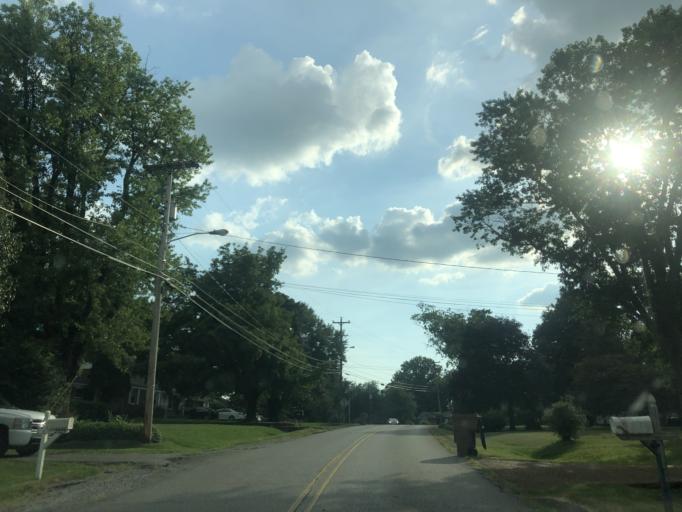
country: US
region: Tennessee
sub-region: Davidson County
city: Lakewood
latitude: 36.1583
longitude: -86.6769
